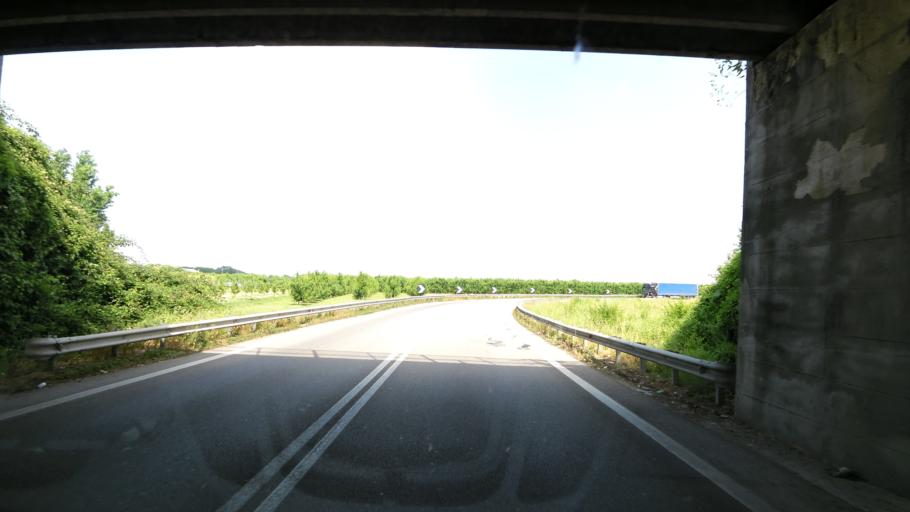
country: IT
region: Emilia-Romagna
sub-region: Forli-Cesena
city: Santa Maria Nuova
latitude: 44.1911
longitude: 12.2242
